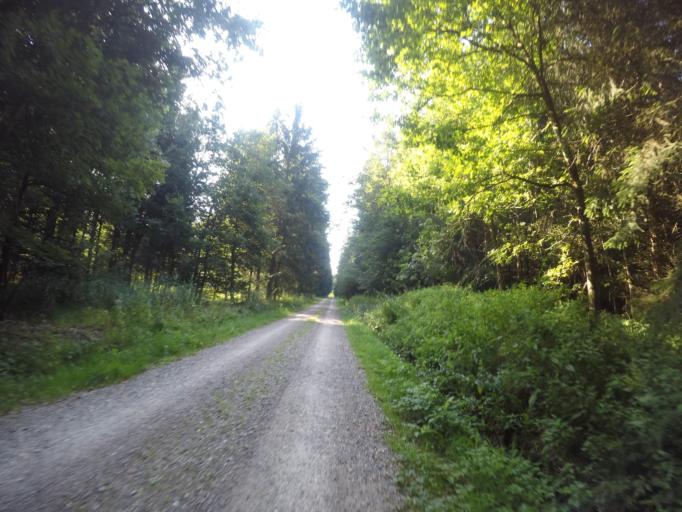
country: DE
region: Baden-Wuerttemberg
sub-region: Tuebingen Region
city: Schnurpflingen
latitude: 48.2508
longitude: 10.0076
